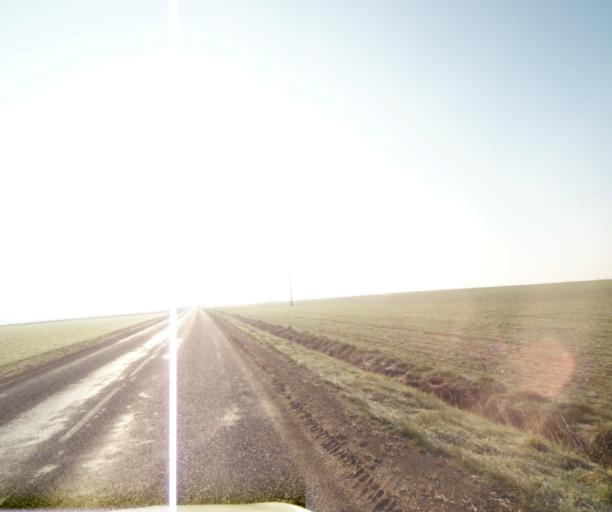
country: FR
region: Champagne-Ardenne
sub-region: Departement de la Haute-Marne
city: Montier-en-Der
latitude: 48.5002
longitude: 4.7510
